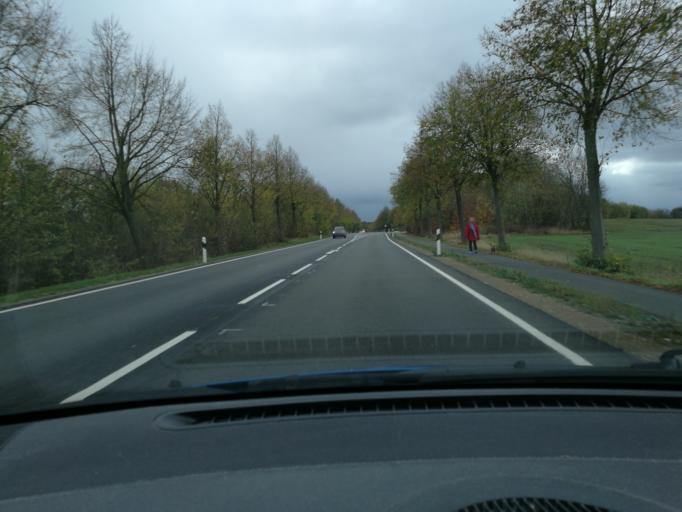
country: DE
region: Schleswig-Holstein
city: Harmsdorf
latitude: 53.6897
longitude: 10.7296
